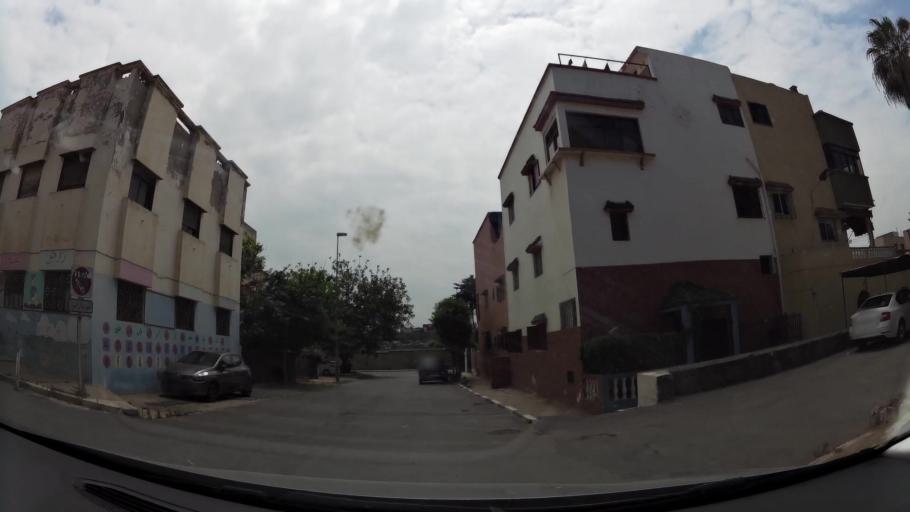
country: MA
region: Rabat-Sale-Zemmour-Zaer
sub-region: Skhirate-Temara
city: Temara
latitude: 33.9841
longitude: -6.8891
